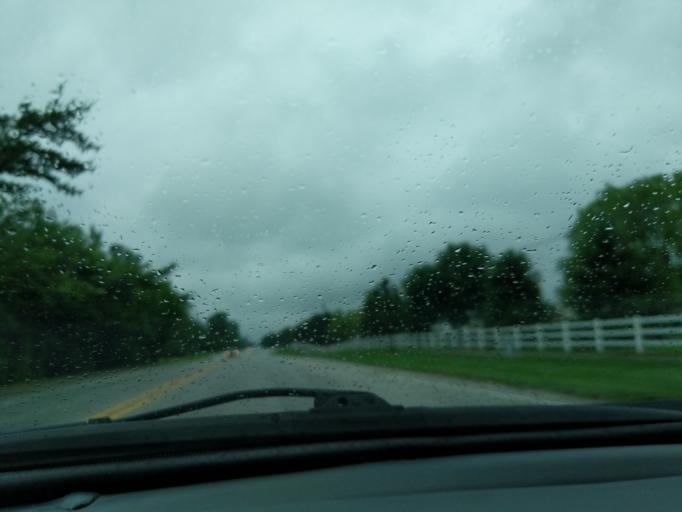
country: US
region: Indiana
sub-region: Hamilton County
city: Noblesville
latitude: 40.0633
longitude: -86.0559
